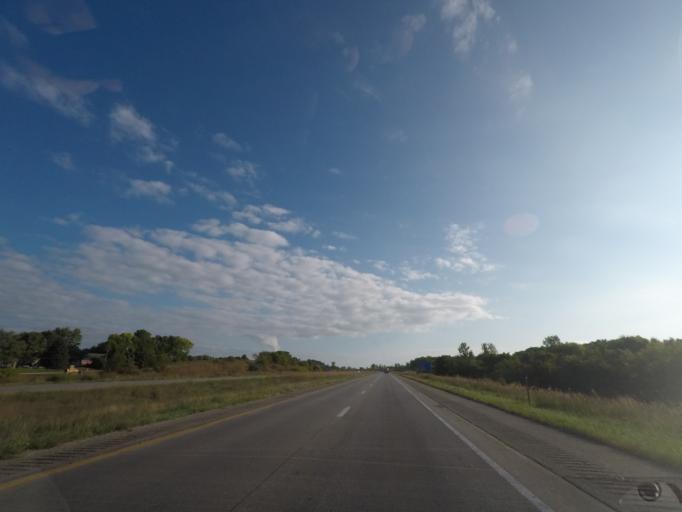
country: US
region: Iowa
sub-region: Polk County
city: Pleasant Hill
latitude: 41.5832
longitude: -93.5064
